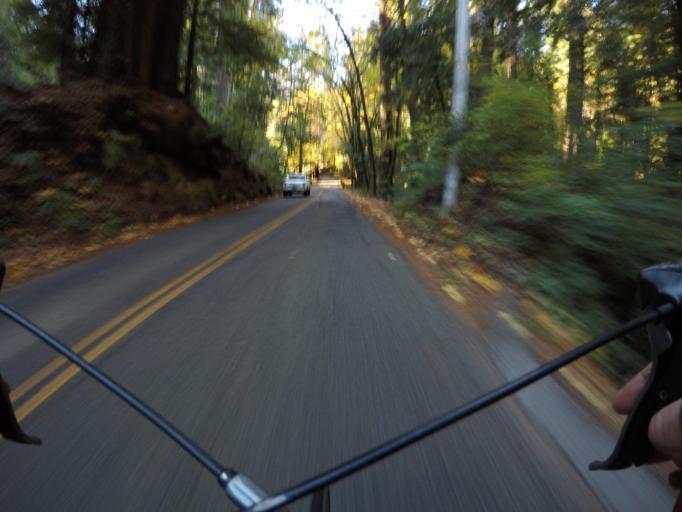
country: US
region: California
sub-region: Santa Cruz County
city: Scotts Valley
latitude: 37.0973
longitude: -121.9959
